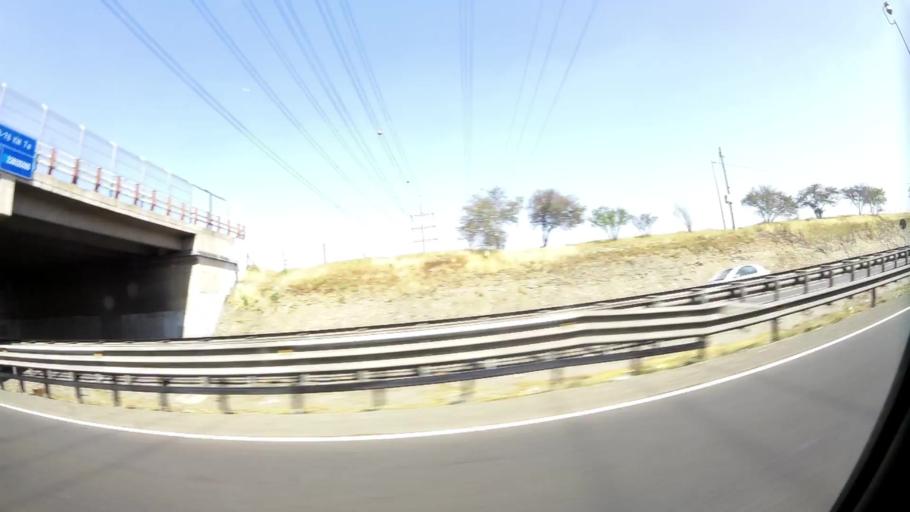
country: CL
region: Santiago Metropolitan
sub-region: Provincia de Santiago
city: Lo Prado
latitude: -33.4840
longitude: -70.7319
